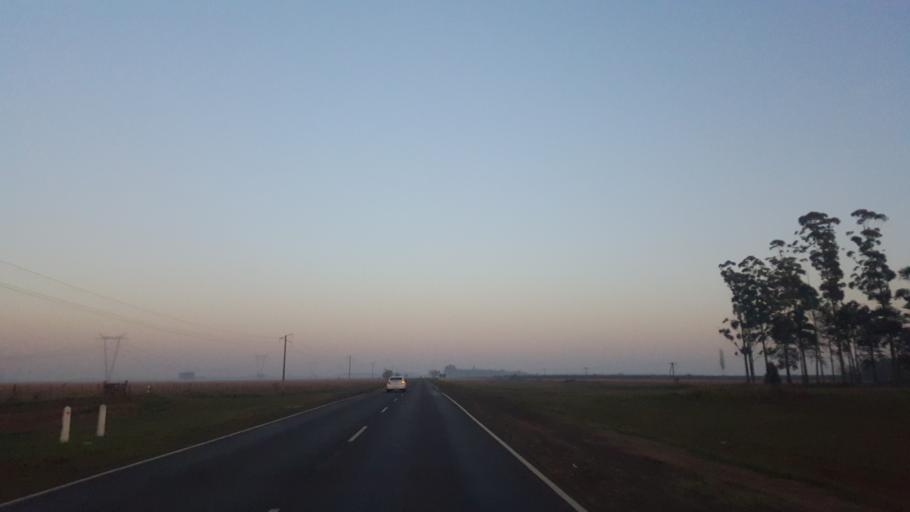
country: AR
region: Corrientes
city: Ituzaingo
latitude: -27.5986
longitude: -56.4609
